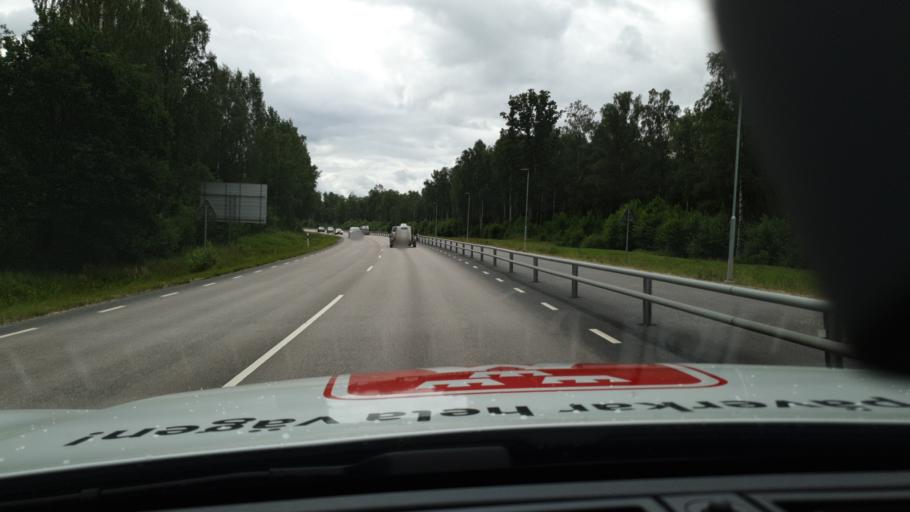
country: SE
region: Kronoberg
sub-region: Alvesta Kommun
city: Alvesta
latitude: 56.9179
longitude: 14.5544
